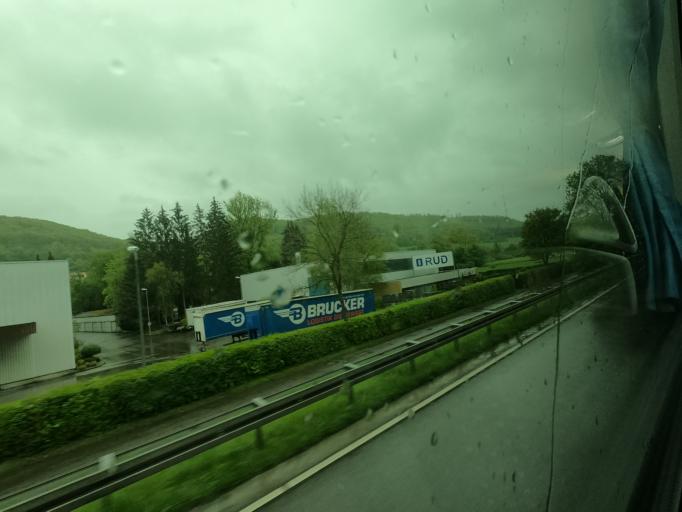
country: DE
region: Baden-Wuerttemberg
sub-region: Regierungsbezirk Stuttgart
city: Oberkochen
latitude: 48.8046
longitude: 10.1252
